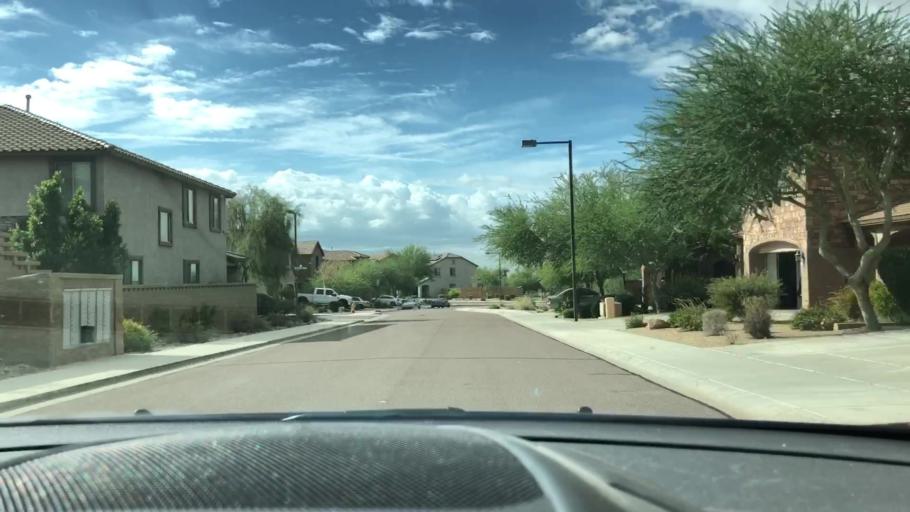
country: US
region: Arizona
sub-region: Maricopa County
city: Sun City West
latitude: 33.7390
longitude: -112.2548
